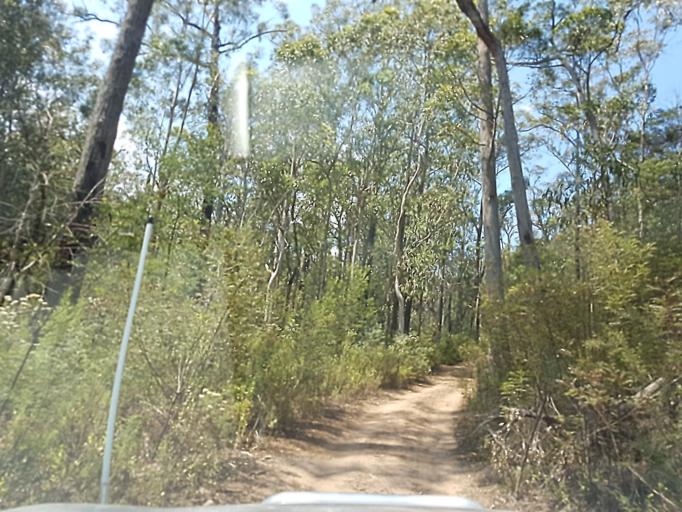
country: AU
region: Victoria
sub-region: East Gippsland
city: Lakes Entrance
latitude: -37.4045
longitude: 148.3152
